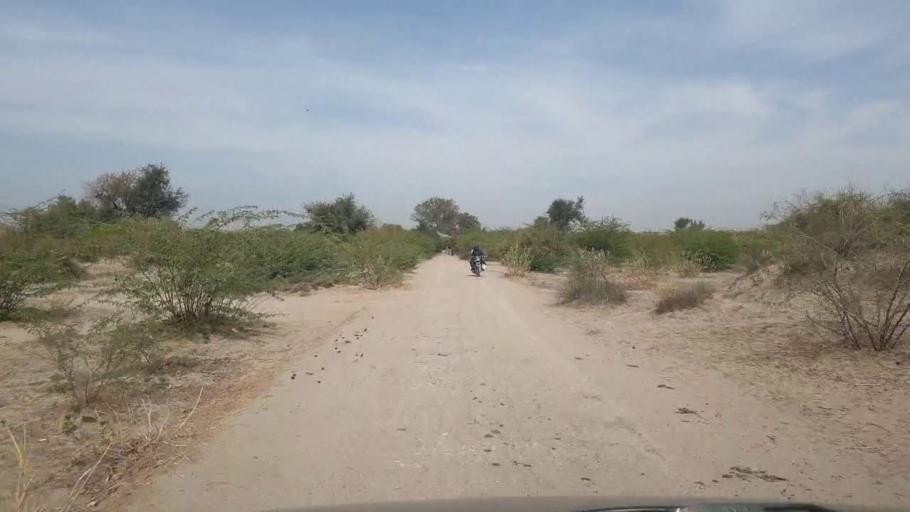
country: PK
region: Sindh
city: Umarkot
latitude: 25.2574
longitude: 69.7244
